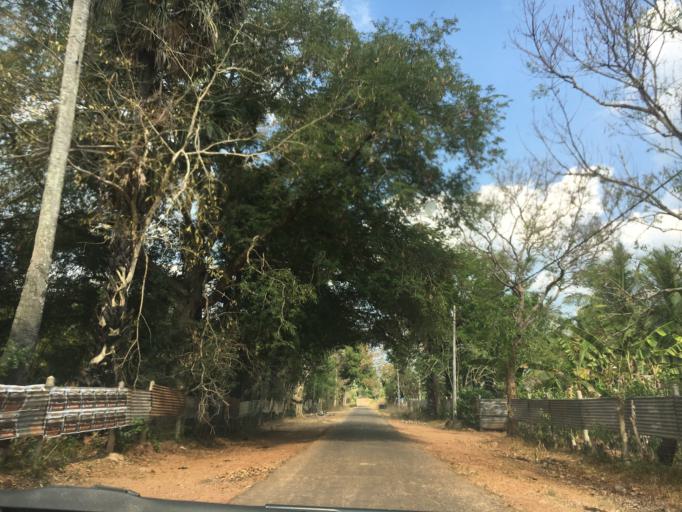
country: LK
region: Northern Province
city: Kilinochchi
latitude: 9.1405
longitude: 80.4441
